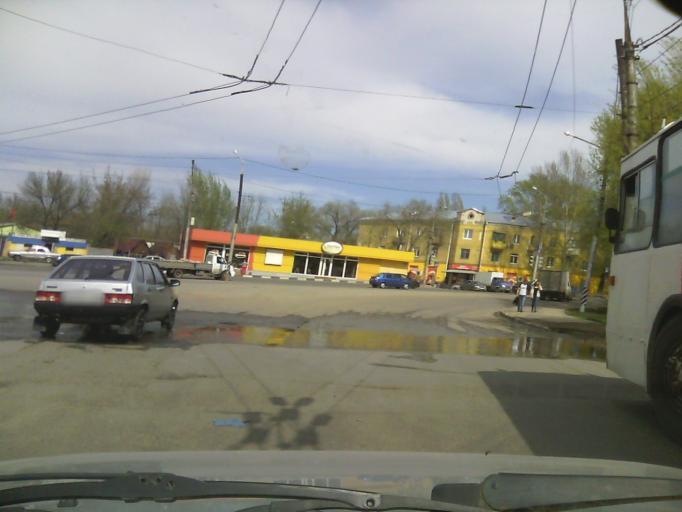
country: RU
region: Saratov
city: Sokolovyy
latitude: 51.6080
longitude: 45.9071
